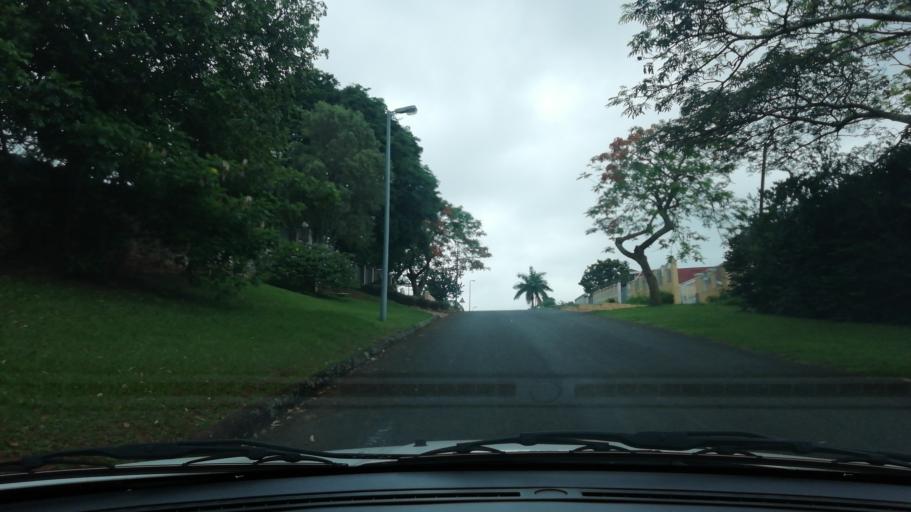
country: ZA
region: KwaZulu-Natal
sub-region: uThungulu District Municipality
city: Empangeni
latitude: -28.7661
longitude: 31.9015
